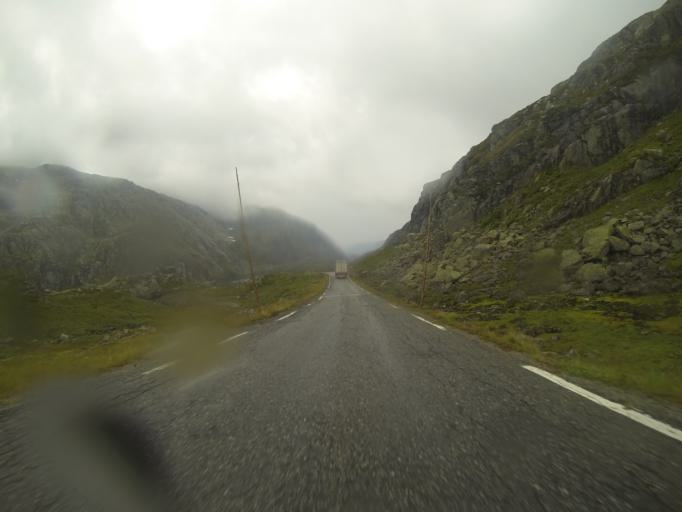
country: NO
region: Hordaland
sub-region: Odda
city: Odda
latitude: 59.7575
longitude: 6.7132
